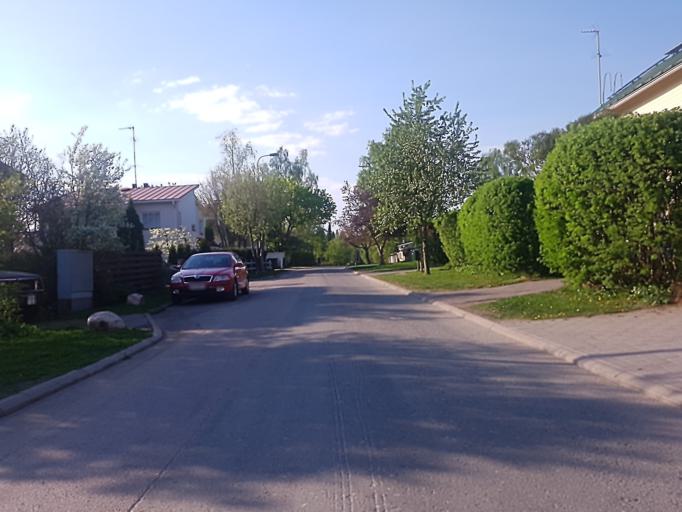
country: FI
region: Uusimaa
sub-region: Helsinki
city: Helsinki
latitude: 60.2479
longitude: 24.9310
